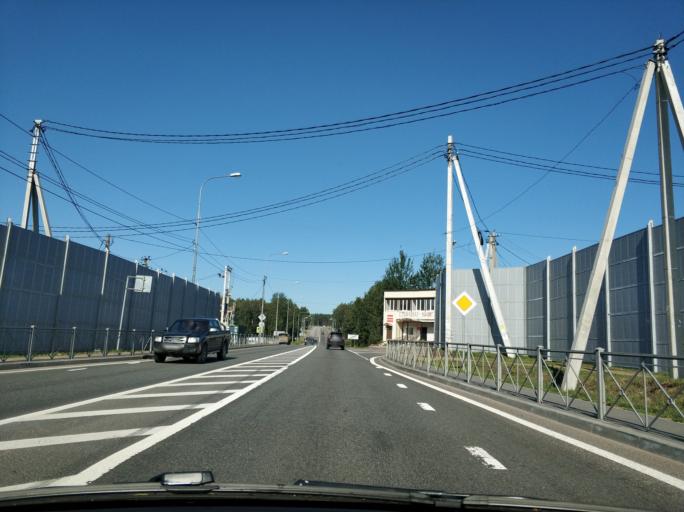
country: RU
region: Leningrad
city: Sapernoye
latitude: 60.6822
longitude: 29.9987
